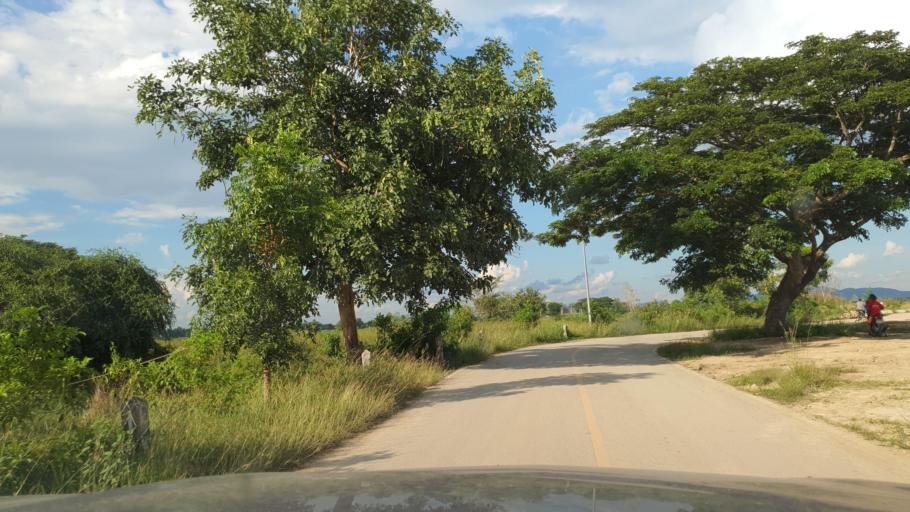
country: TH
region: Phayao
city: Phayao
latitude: 19.1843
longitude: 99.8549
